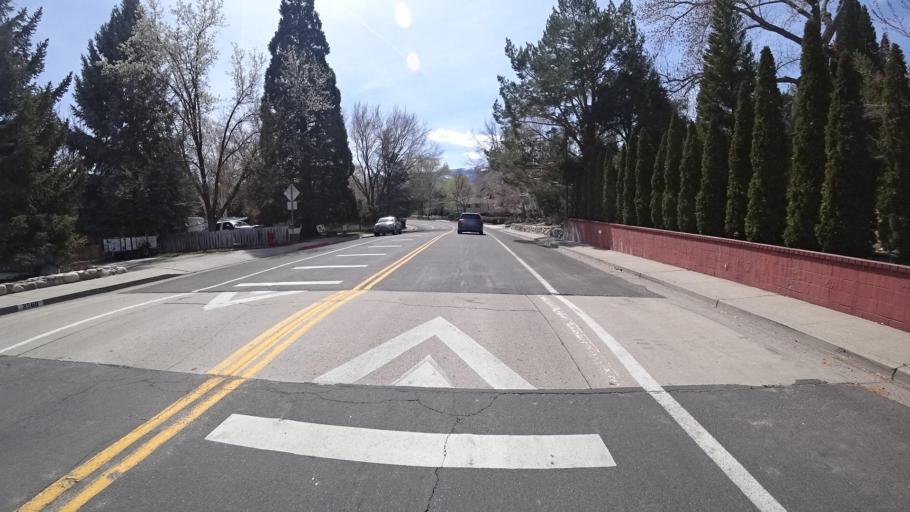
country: US
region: Nevada
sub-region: Washoe County
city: Reno
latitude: 39.5005
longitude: -119.8253
